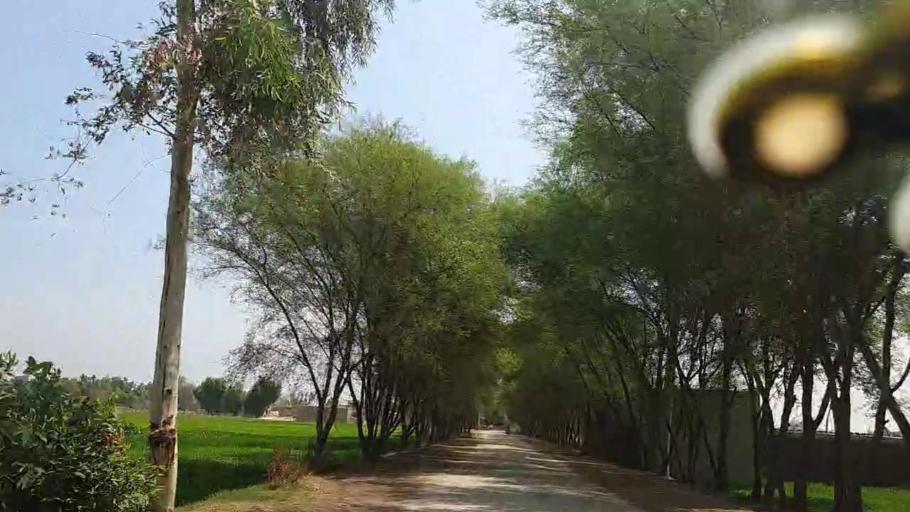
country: PK
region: Sindh
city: Rustam jo Goth
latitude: 28.1088
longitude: 68.8789
